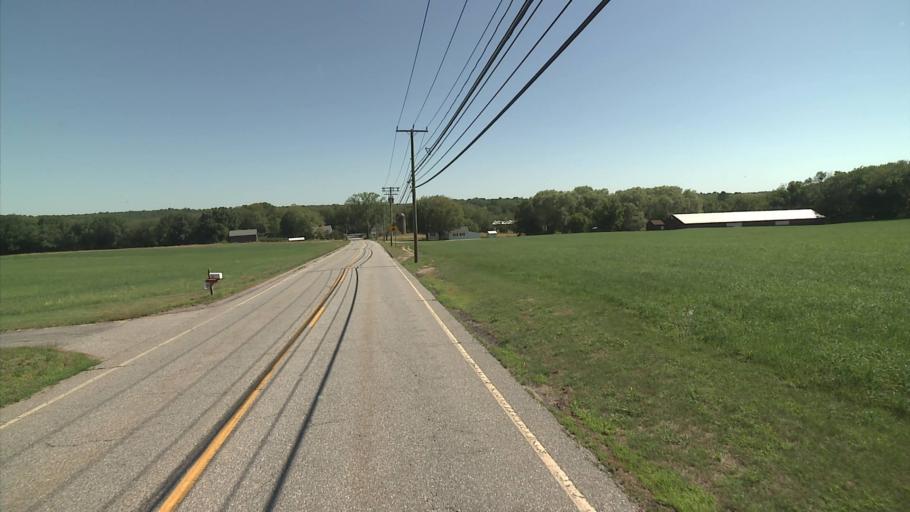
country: US
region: Connecticut
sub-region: New London County
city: Colchester
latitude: 41.6145
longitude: -72.2732
